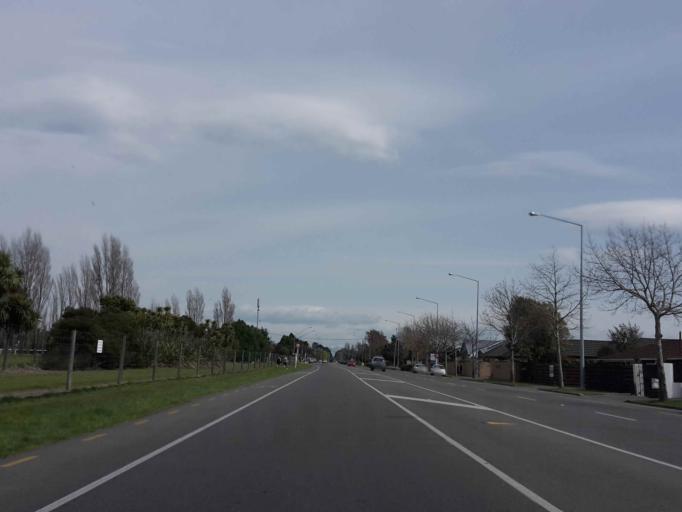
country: NZ
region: Canterbury
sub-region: Selwyn District
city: Prebbleton
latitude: -43.5223
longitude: 172.5405
